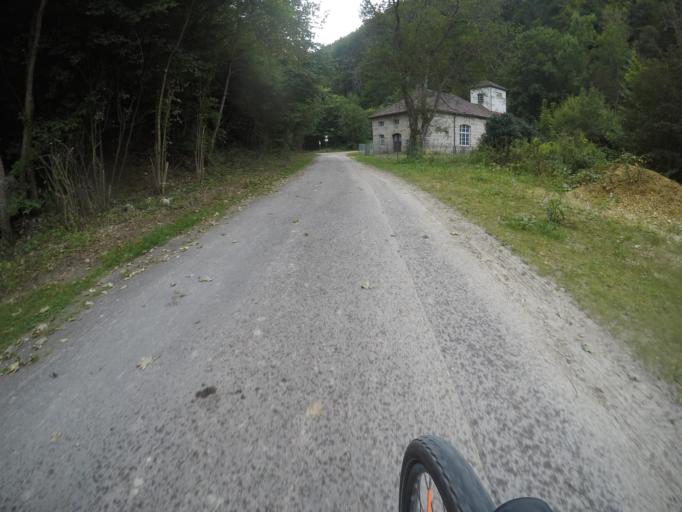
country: DE
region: Baden-Wuerttemberg
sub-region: Tuebingen Region
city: Munsingen
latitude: 48.4437
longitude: 9.4617
